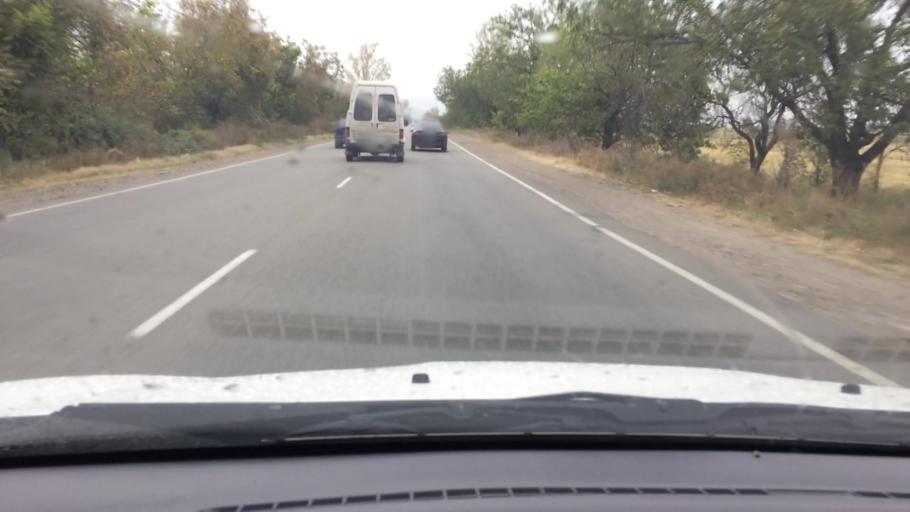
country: GE
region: Kvemo Kartli
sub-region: Marneuli
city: Marneuli
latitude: 41.5529
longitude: 44.7763
